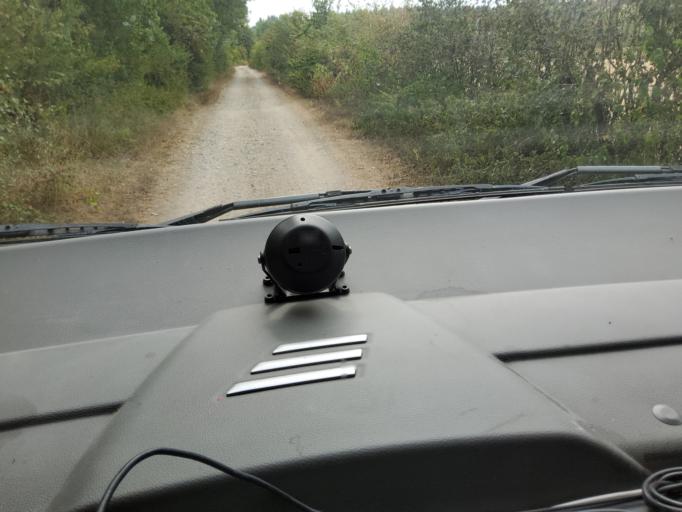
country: FR
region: Franche-Comte
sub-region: Departement du Jura
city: Choisey
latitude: 47.0147
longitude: 5.4809
